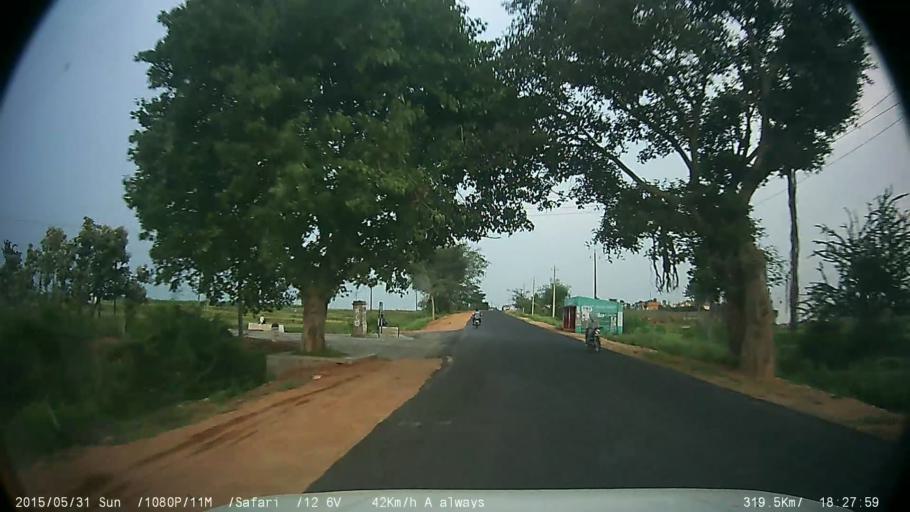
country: IN
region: Karnataka
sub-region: Mysore
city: Nanjangud
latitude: 12.1218
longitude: 76.7187
